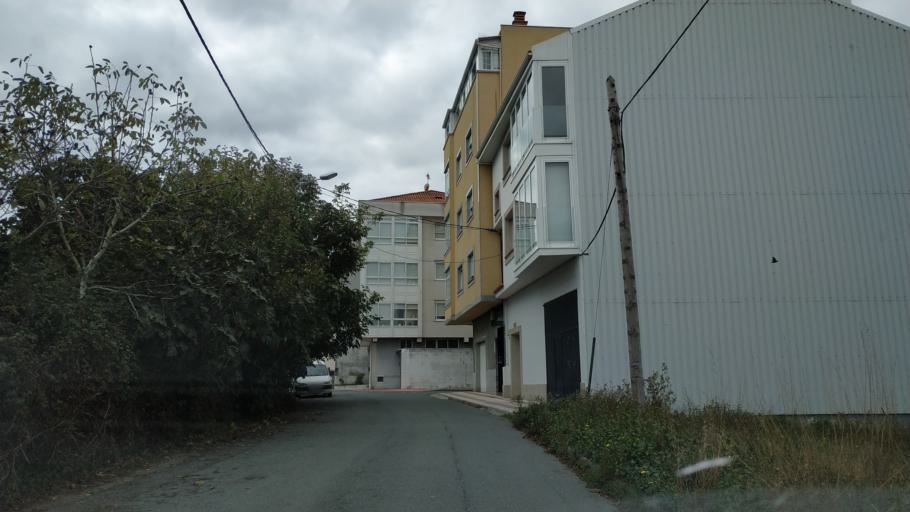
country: ES
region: Galicia
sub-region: Provincia da Coruna
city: Arteixo
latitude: 43.3017
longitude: -8.5106
